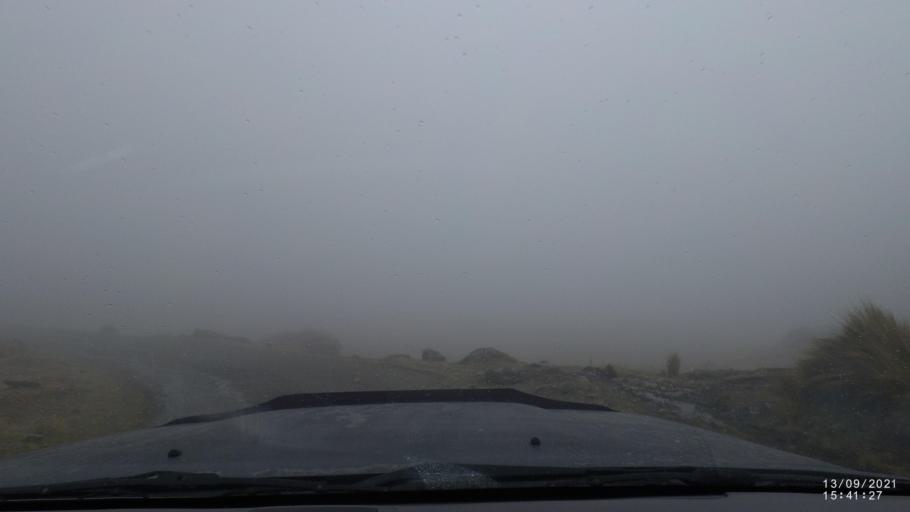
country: BO
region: Cochabamba
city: Colomi
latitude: -17.3233
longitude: -65.7169
